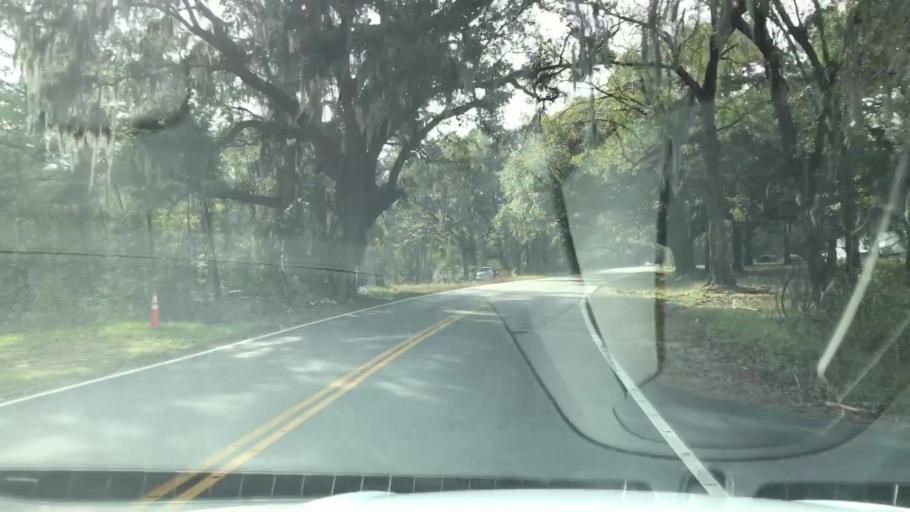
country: US
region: South Carolina
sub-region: Charleston County
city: Folly Beach
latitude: 32.6991
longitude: -80.0144
